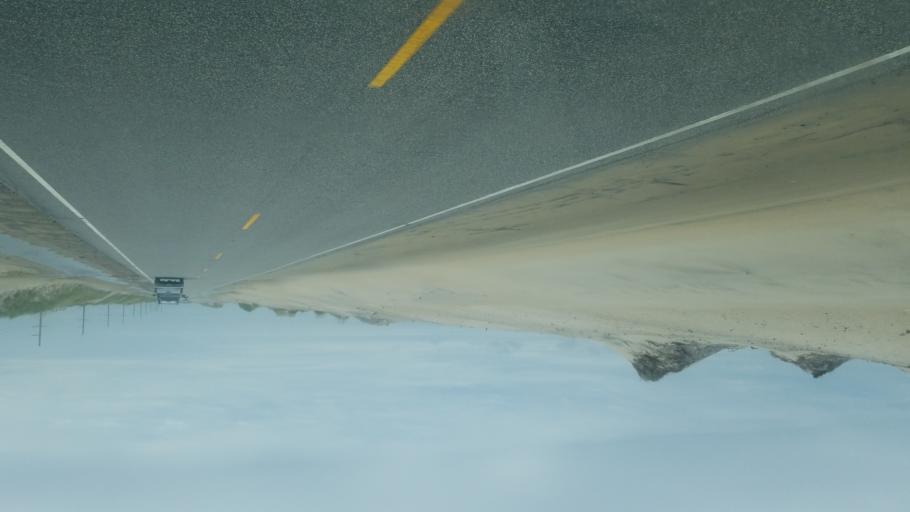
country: US
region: North Carolina
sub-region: Dare County
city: Wanchese
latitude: 35.7507
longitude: -75.5089
